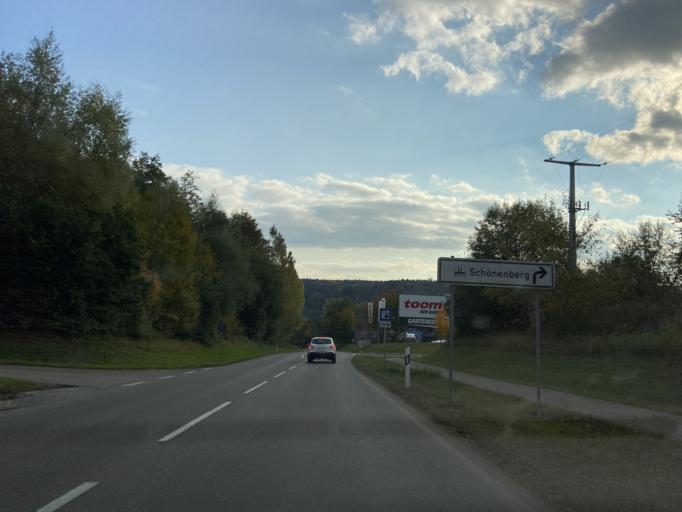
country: DE
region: Baden-Wuerttemberg
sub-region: Tuebingen Region
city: Sigmaringen
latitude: 48.0822
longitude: 9.2394
